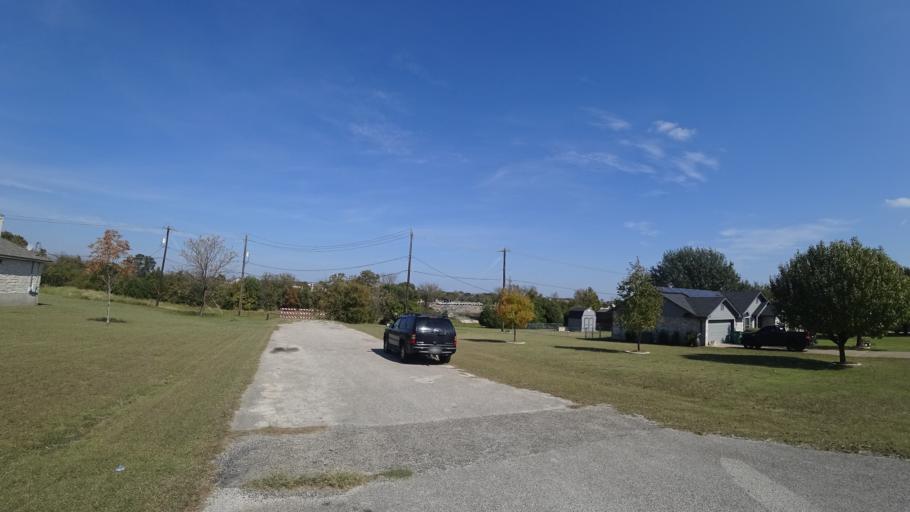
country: US
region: Texas
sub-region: Travis County
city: Pflugerville
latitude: 30.4209
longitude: -97.6241
